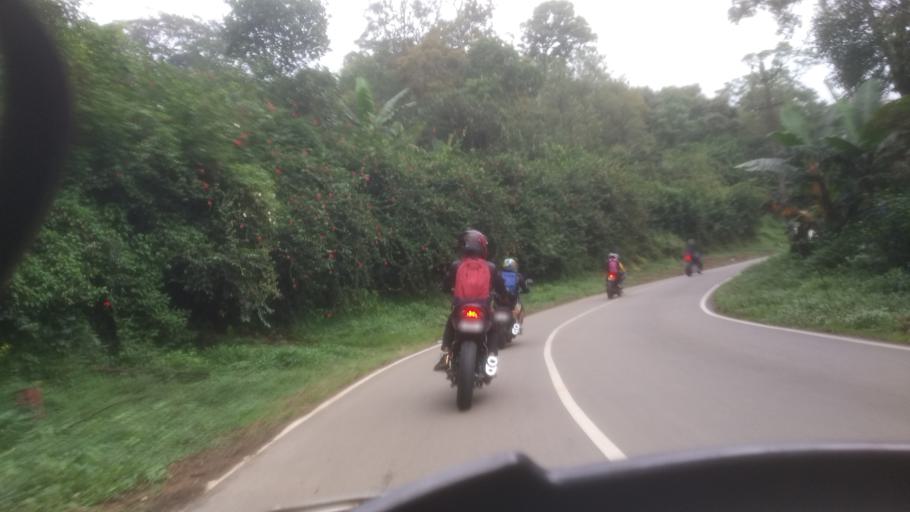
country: IN
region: Tamil Nadu
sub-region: Theni
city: Kombai
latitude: 9.8930
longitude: 77.2027
